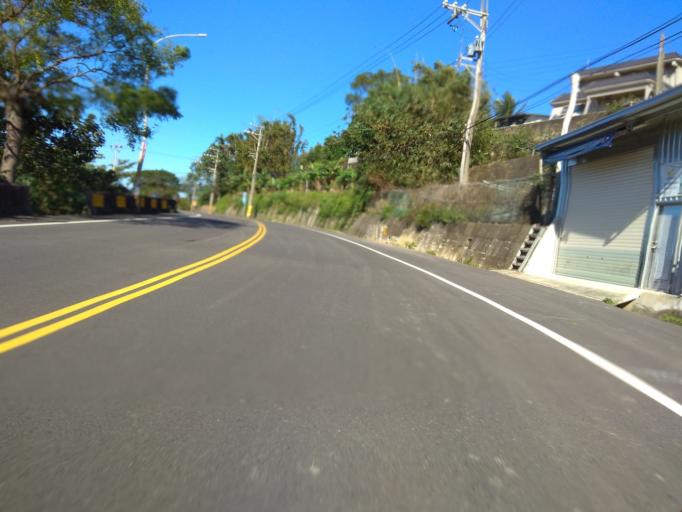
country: TW
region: Taiwan
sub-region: Hsinchu
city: Zhubei
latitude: 24.8456
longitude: 121.1205
